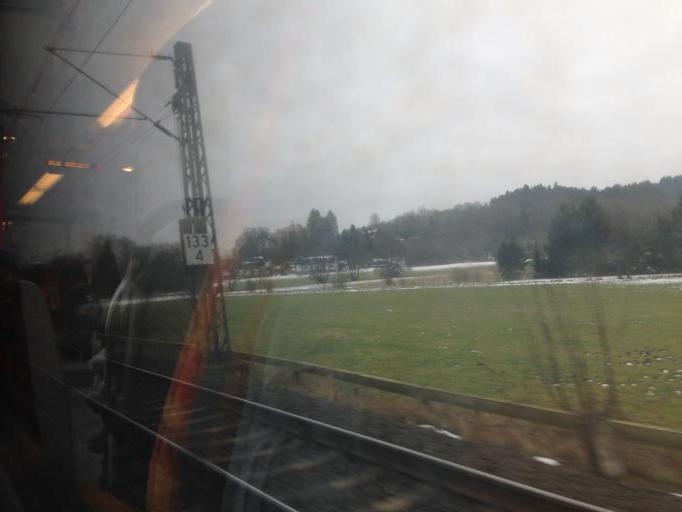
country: DE
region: Hesse
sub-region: Regierungsbezirk Giessen
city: Sinn
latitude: 50.6630
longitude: 8.3209
